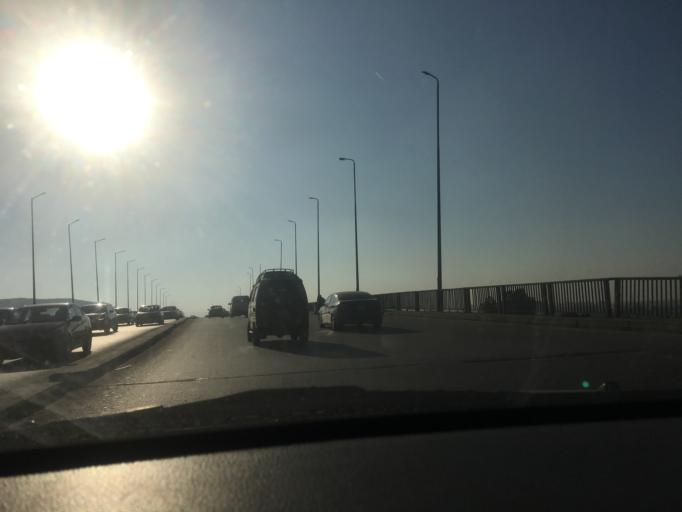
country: EG
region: Muhafazat al Qahirah
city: Cairo
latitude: 30.0096
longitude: 31.2687
